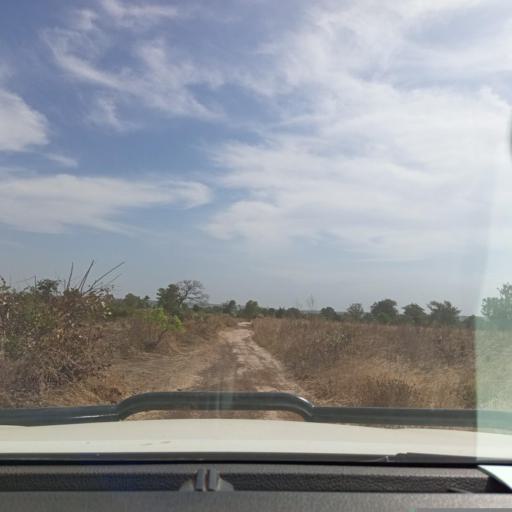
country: ML
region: Koulikoro
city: Kati
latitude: 12.7325
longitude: -8.2540
